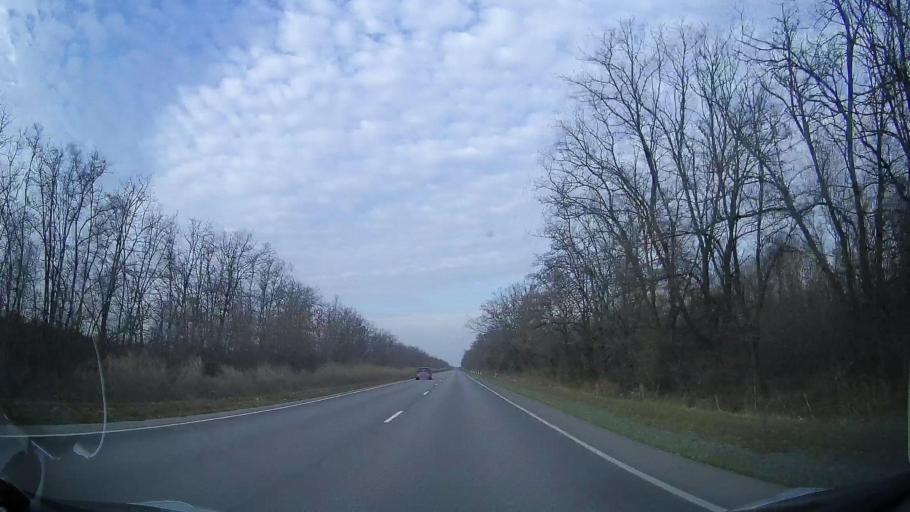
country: RU
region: Rostov
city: Bagayevskaya
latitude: 47.1165
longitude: 40.2767
